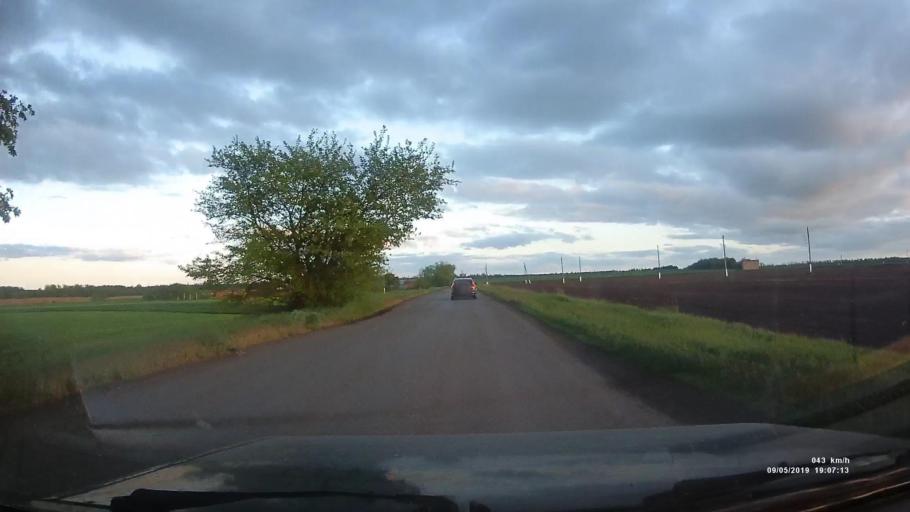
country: RU
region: Krasnodarskiy
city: Kanelovskaya
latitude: 46.7354
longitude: 39.1968
